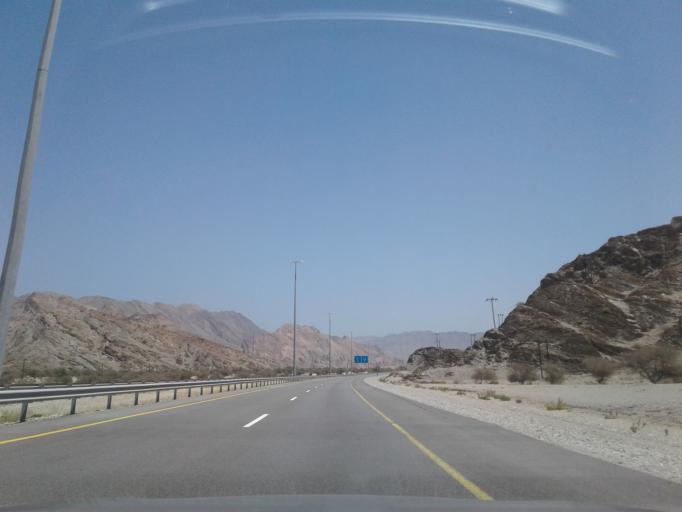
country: OM
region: Muhafazat Masqat
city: Muscat
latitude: 23.3633
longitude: 58.6615
